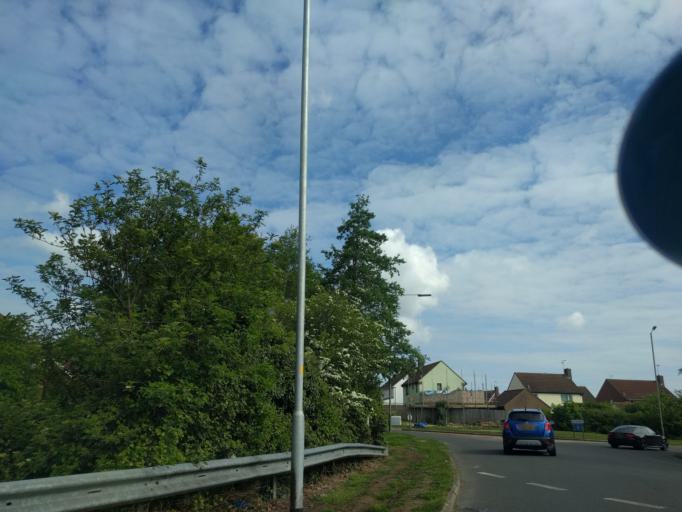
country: GB
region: England
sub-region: Wiltshire
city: Lydiard Tregoze
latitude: 51.5603
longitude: -1.8303
